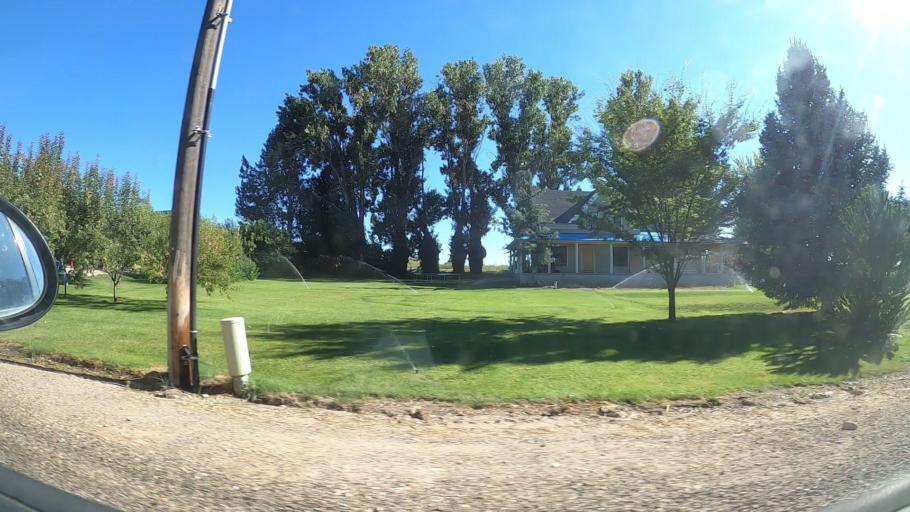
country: US
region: Idaho
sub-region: Canyon County
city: Nampa
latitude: 43.5472
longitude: -116.6069
